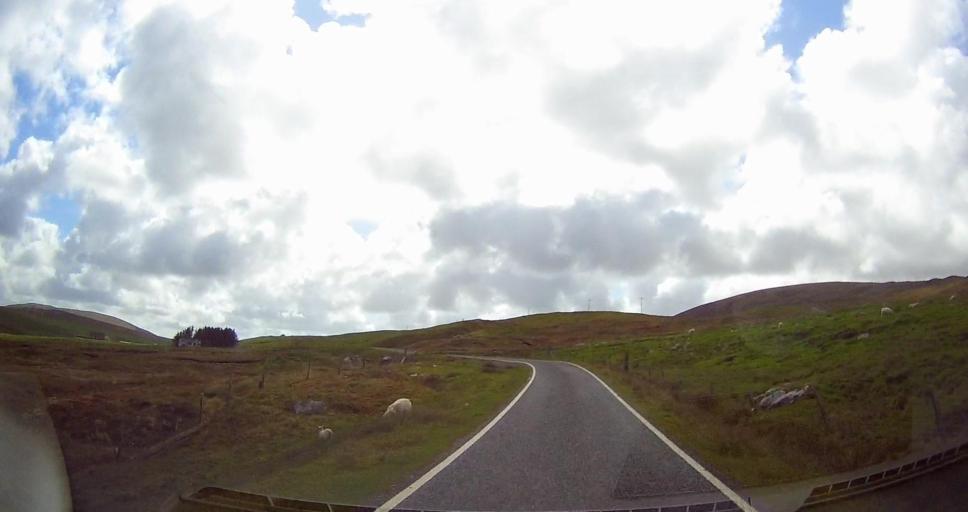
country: GB
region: Scotland
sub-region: Shetland Islands
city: Lerwick
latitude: 60.5351
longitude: -1.3584
